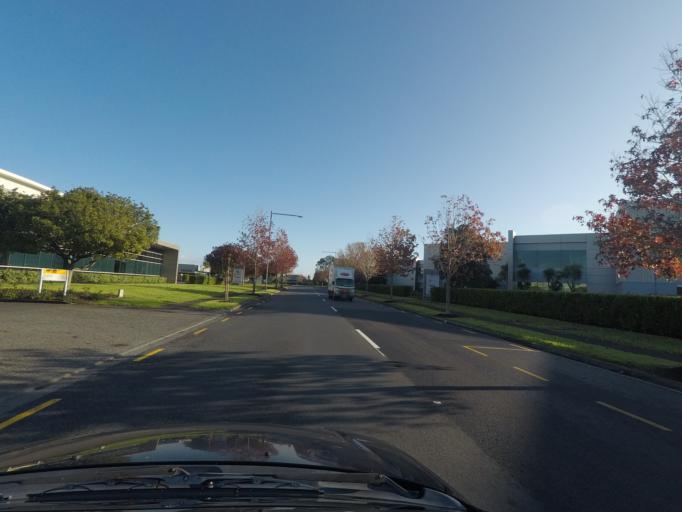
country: NZ
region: Auckland
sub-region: Auckland
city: Manukau City
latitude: -36.9398
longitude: 174.8777
